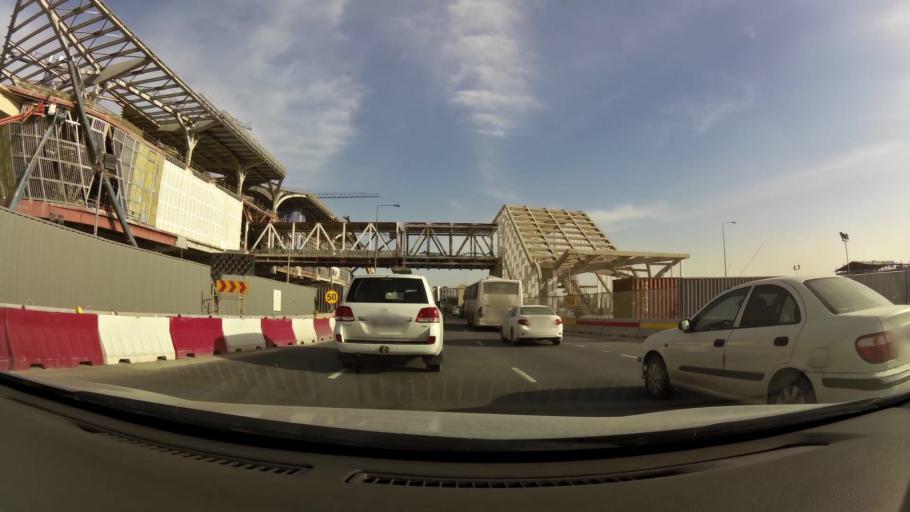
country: QA
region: Al Wakrah
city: Al Wakrah
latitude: 25.1943
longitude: 51.5950
